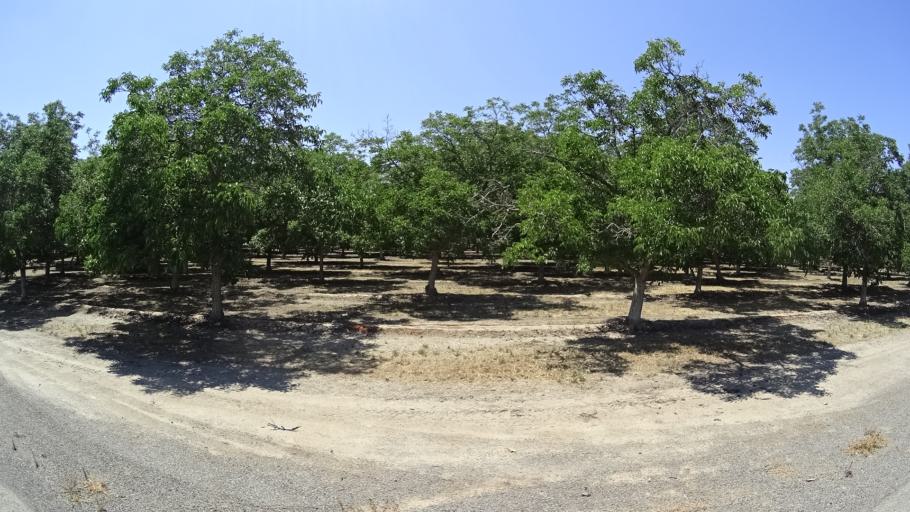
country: US
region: California
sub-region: Fresno County
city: Laton
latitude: 36.4024
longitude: -119.6955
